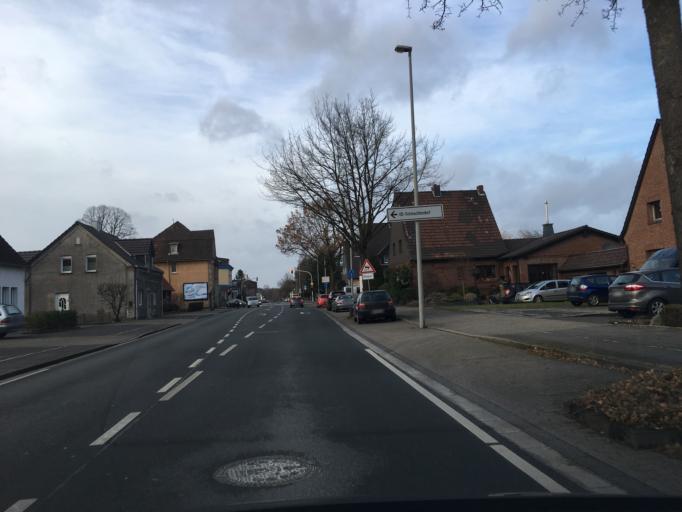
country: DE
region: North Rhine-Westphalia
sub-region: Regierungsbezirk Dusseldorf
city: Oberhausen
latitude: 51.5519
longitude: 6.8468
